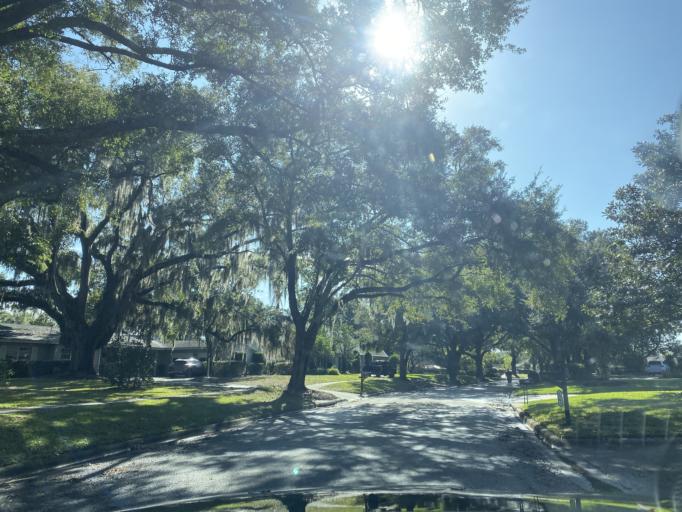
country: US
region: Florida
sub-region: Orange County
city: Azalea Park
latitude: 28.5311
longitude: -81.2636
